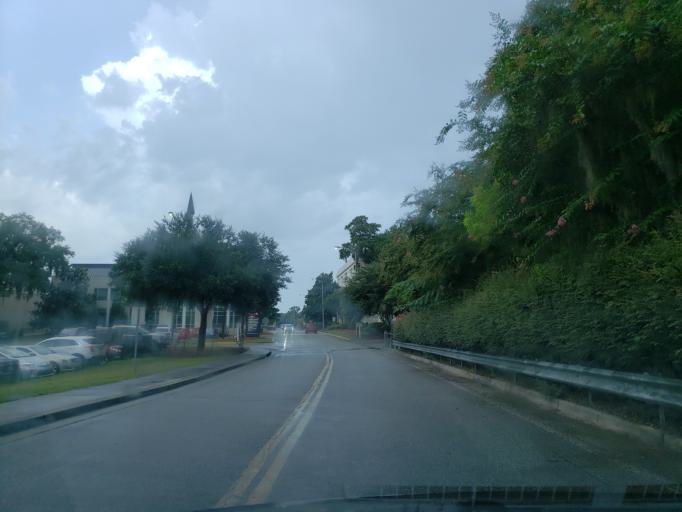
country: US
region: Georgia
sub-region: Chatham County
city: Thunderbolt
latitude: 32.0310
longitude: -81.0862
